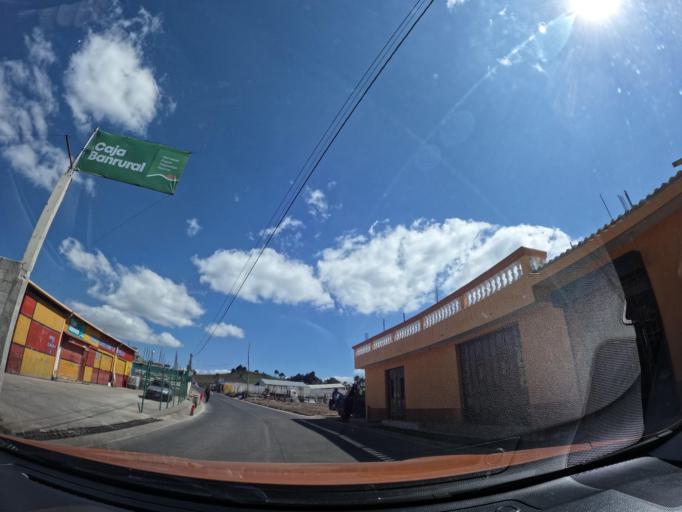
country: GT
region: Chimaltenango
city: Patzun
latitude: 14.6545
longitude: -91.0548
